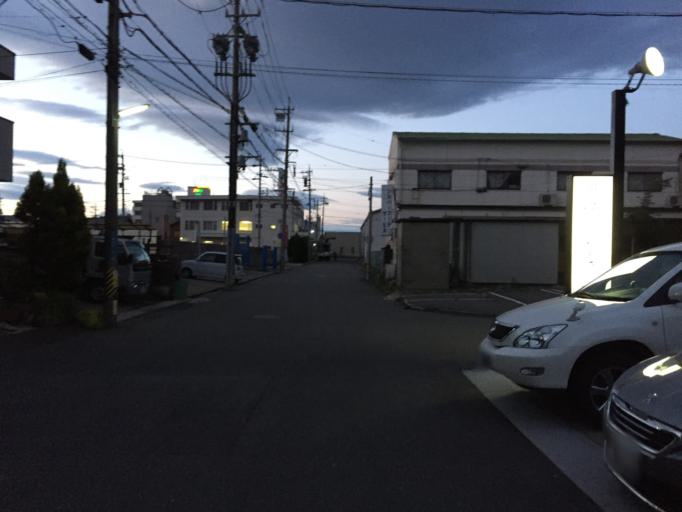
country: JP
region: Mie
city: Yokkaichi
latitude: 34.9583
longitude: 136.6268
